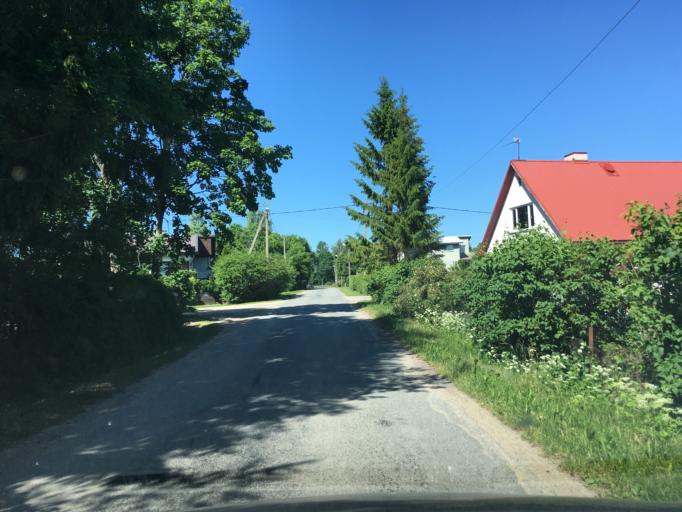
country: EE
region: Harju
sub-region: Raasiku vald
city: Raasiku
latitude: 59.3634
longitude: 25.1734
